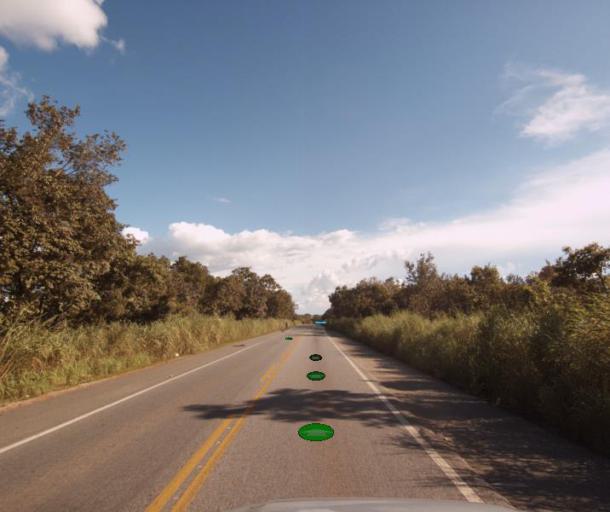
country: BR
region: Goias
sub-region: Porangatu
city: Porangatu
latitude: -13.0653
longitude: -49.1835
